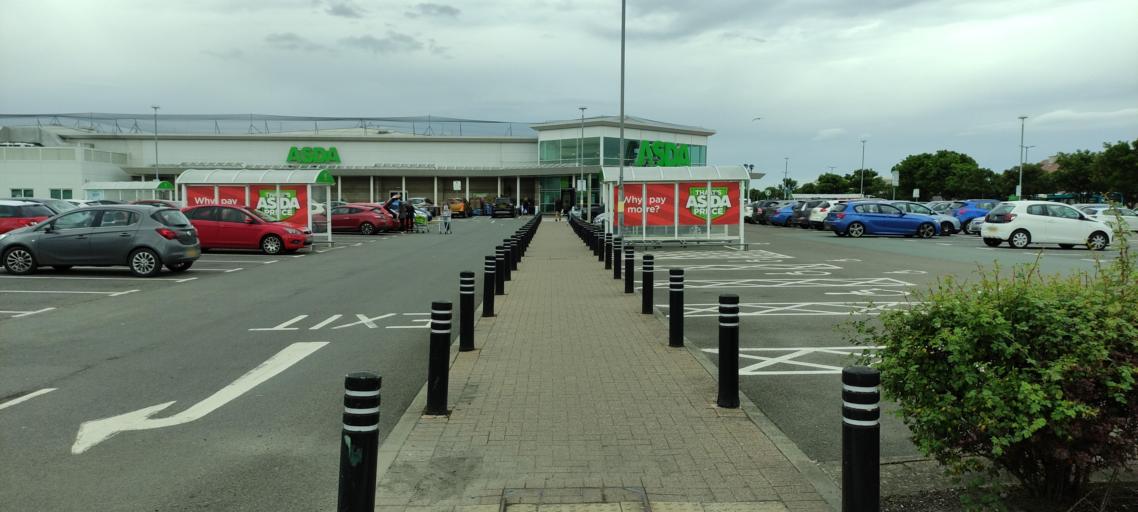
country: GB
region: England
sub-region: Hartlepool
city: Hartlepool
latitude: 54.6884
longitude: -1.2097
